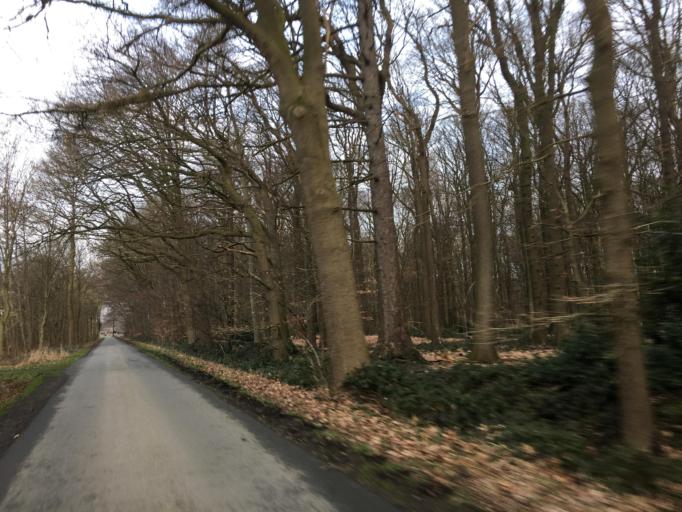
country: DE
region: North Rhine-Westphalia
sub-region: Regierungsbezirk Munster
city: Senden
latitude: 51.9193
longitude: 7.4937
